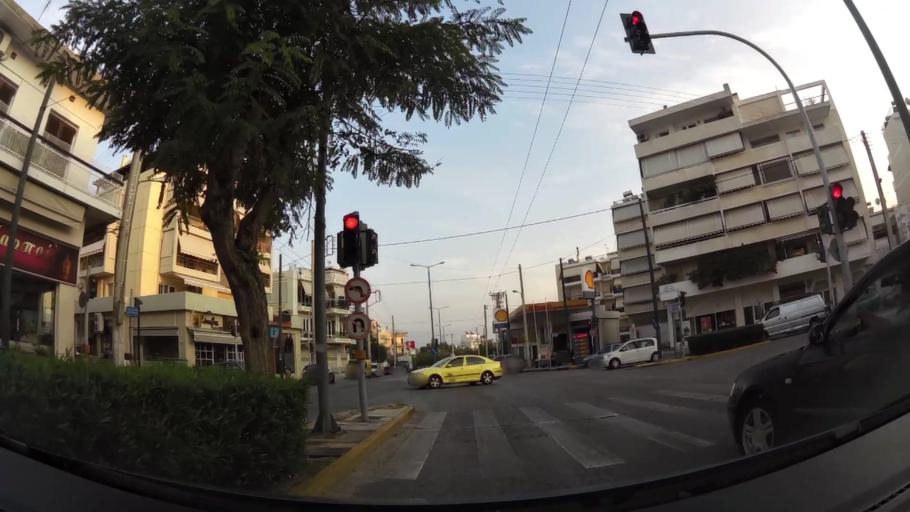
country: GR
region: Attica
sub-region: Nomarchia Athinas
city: Ilion
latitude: 38.0295
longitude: 23.6951
